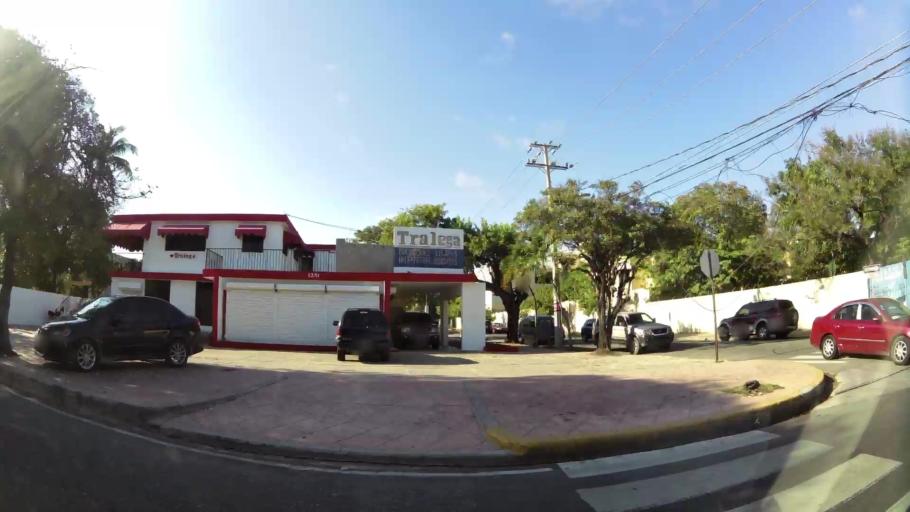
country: DO
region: Nacional
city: La Julia
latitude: 18.4551
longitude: -69.9206
